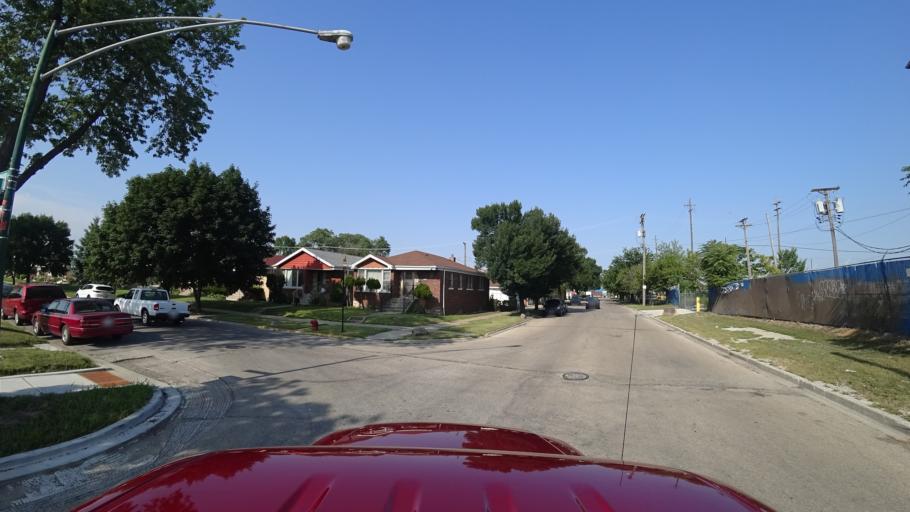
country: US
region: Illinois
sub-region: Cook County
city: Cicero
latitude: 41.8154
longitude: -87.7090
